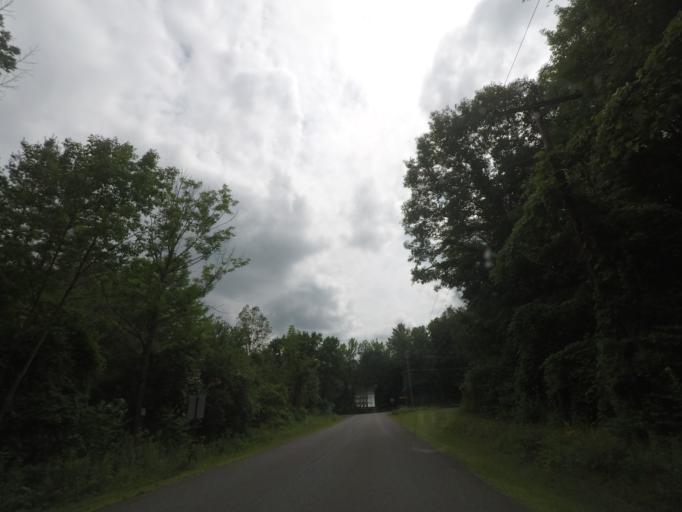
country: US
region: New York
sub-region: Saratoga County
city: Stillwater
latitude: 42.9927
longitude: -73.6903
